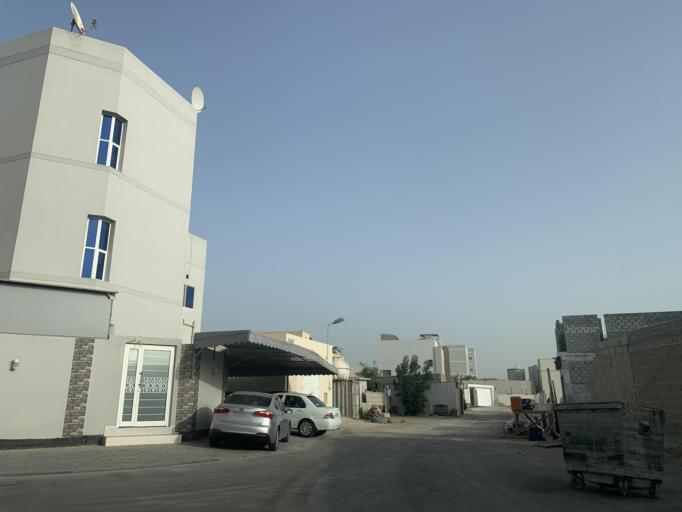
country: BH
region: Northern
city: Madinat `Isa
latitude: 26.1632
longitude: 50.5132
